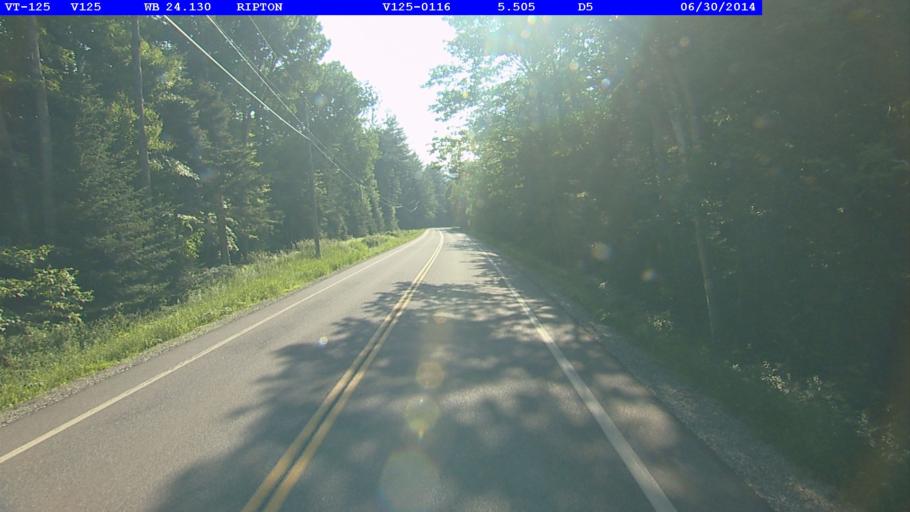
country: US
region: Vermont
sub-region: Rutland County
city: Brandon
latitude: 43.9442
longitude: -72.9722
